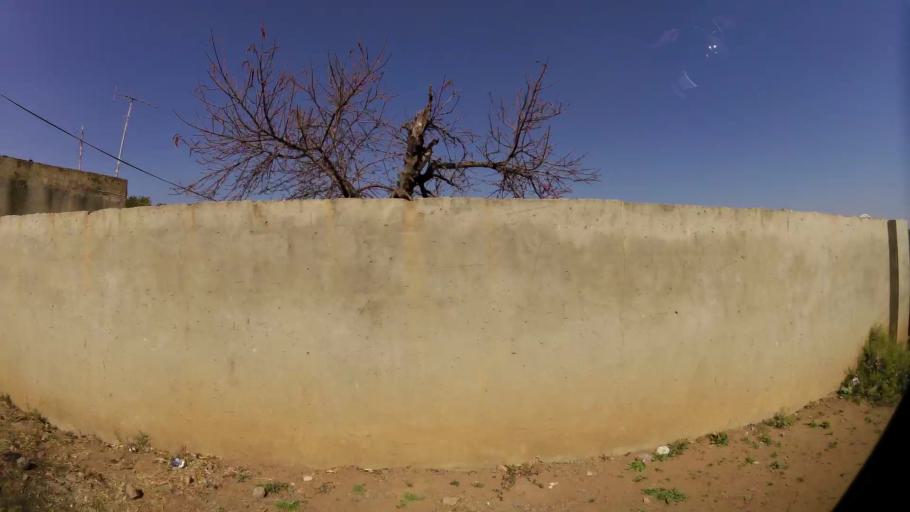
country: ZA
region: Gauteng
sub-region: City of Johannesburg Metropolitan Municipality
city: Soweto
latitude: -26.2522
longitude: 27.9412
